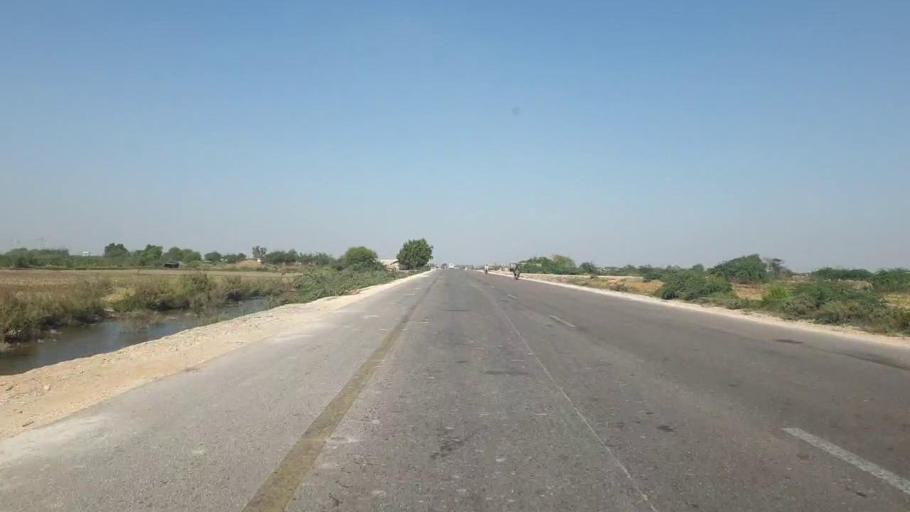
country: PK
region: Sindh
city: Talhar
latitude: 24.8314
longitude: 68.8160
